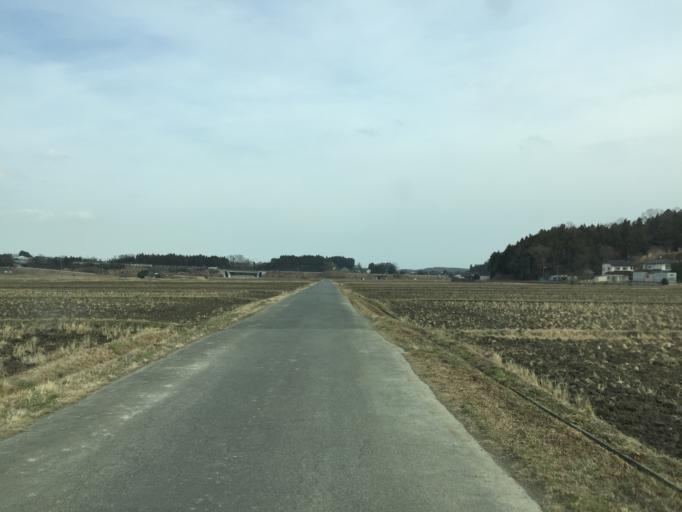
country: JP
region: Ibaraki
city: Kitaibaraki
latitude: 36.8871
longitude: 140.7360
